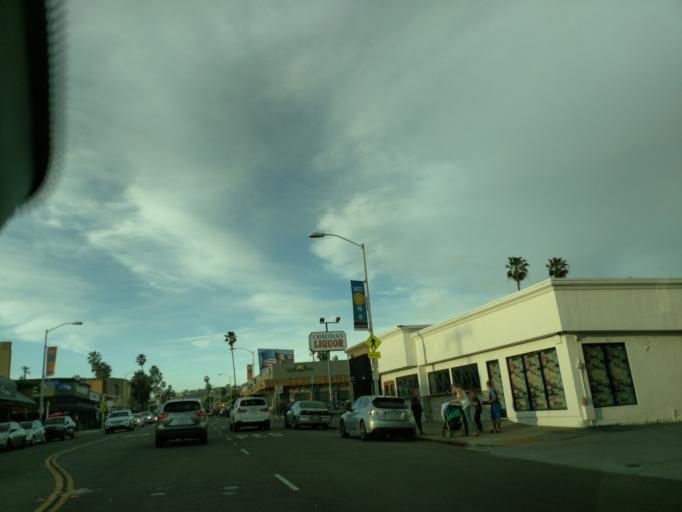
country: US
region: California
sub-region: San Diego County
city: La Jolla
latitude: 32.7979
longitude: -117.2559
